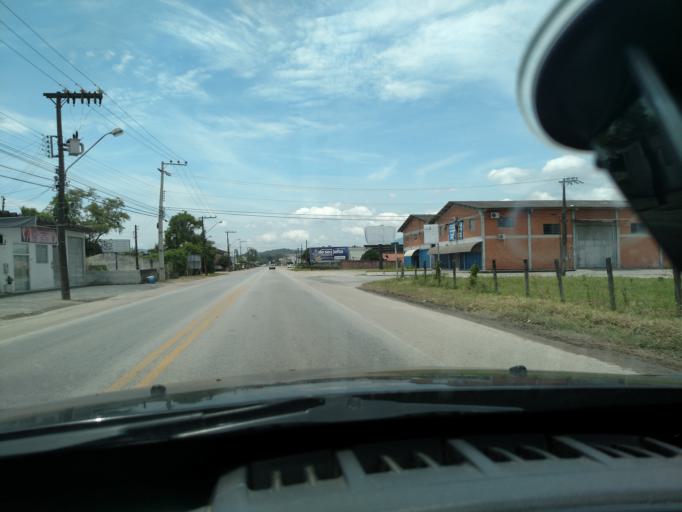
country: BR
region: Santa Catarina
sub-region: Gaspar
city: Gaspar
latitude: -26.9142
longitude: -48.9802
